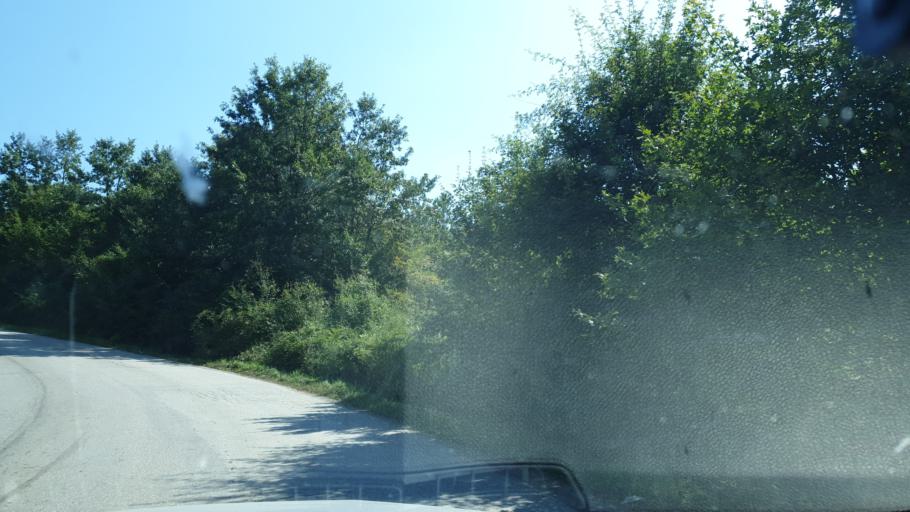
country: RS
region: Central Serbia
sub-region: Zlatiborski Okrug
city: Cajetina
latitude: 43.7012
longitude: 19.8479
